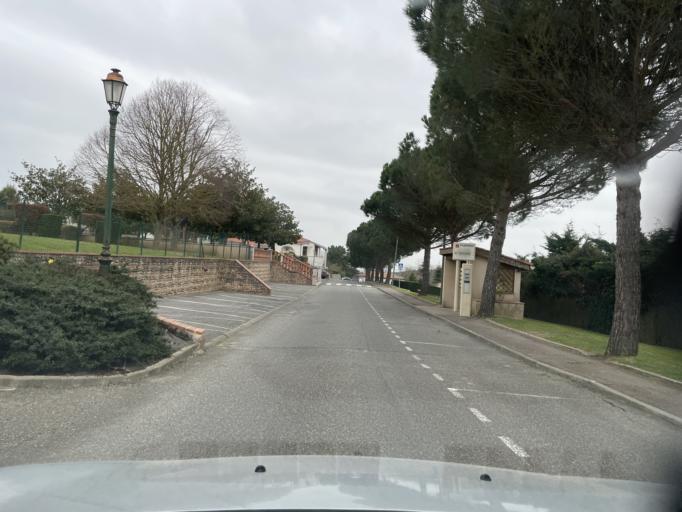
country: FR
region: Midi-Pyrenees
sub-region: Departement du Gers
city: Pujaudran
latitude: 43.5904
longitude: 1.1490
